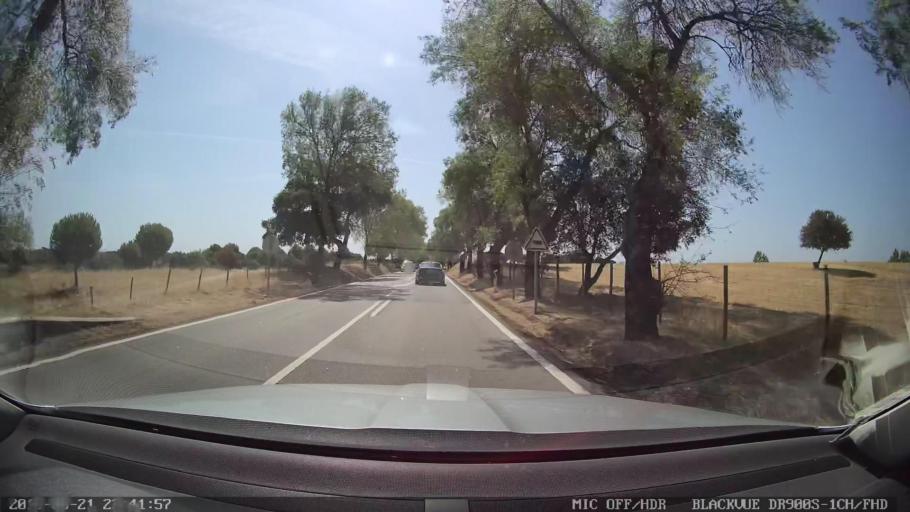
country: PT
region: Castelo Branco
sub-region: Idanha-A-Nova
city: Idanha-a-Nova
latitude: 39.8609
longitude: -7.3164
